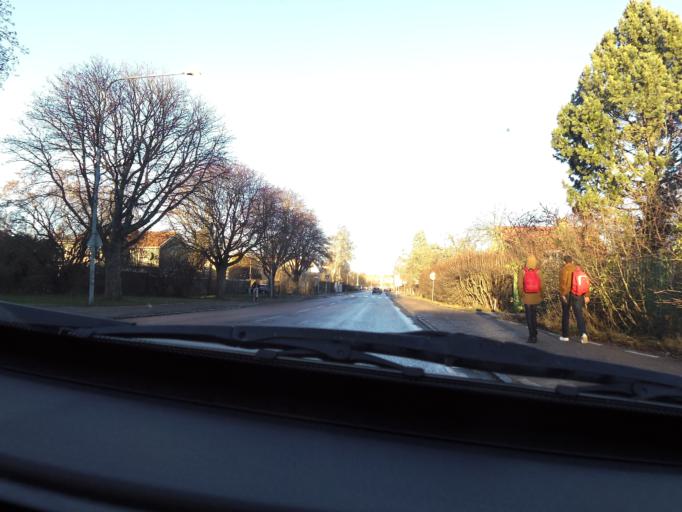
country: SE
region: Gaevleborg
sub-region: Gavle Kommun
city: Gavle
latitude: 60.6689
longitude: 17.1342
